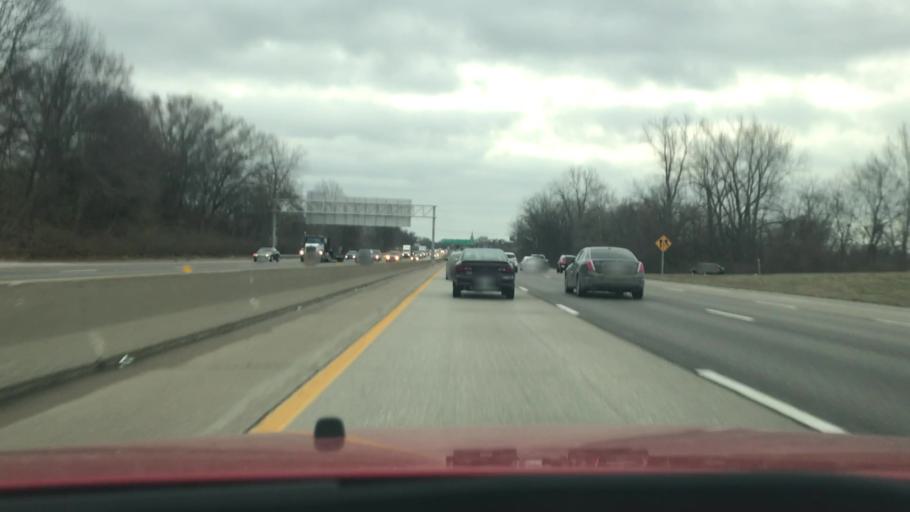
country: US
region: Missouri
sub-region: Saint Charles County
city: Saint Peters
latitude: 38.8012
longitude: -90.6487
